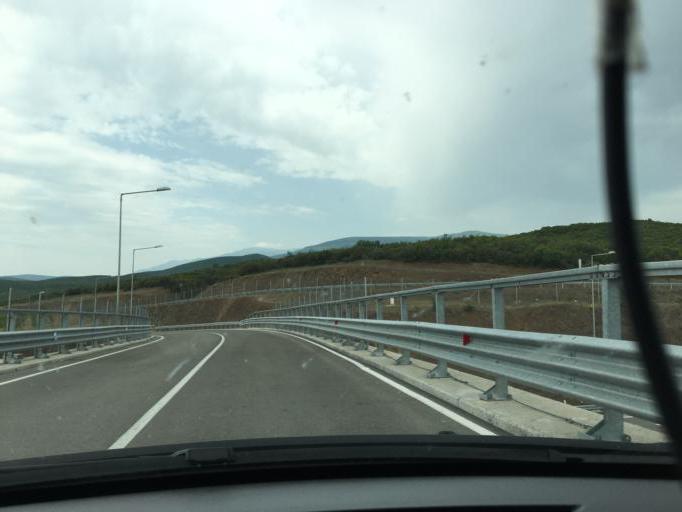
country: MK
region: Gevgelija
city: Miravci
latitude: 41.2979
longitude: 22.4313
